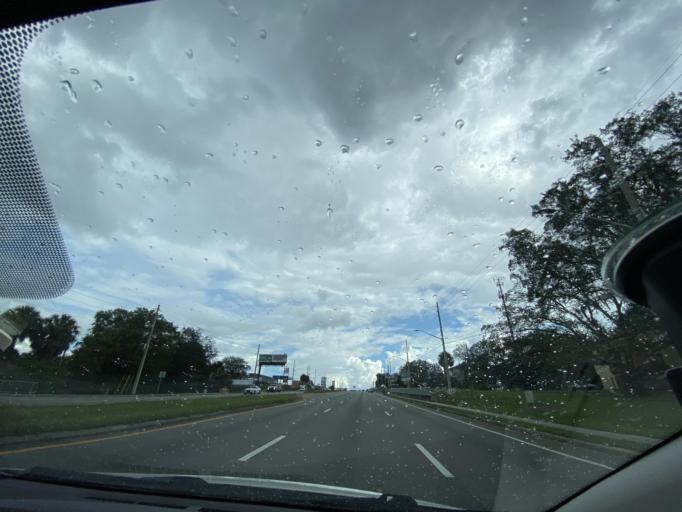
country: US
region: Florida
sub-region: Orange County
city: Orlovista
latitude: 28.5520
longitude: -81.4727
